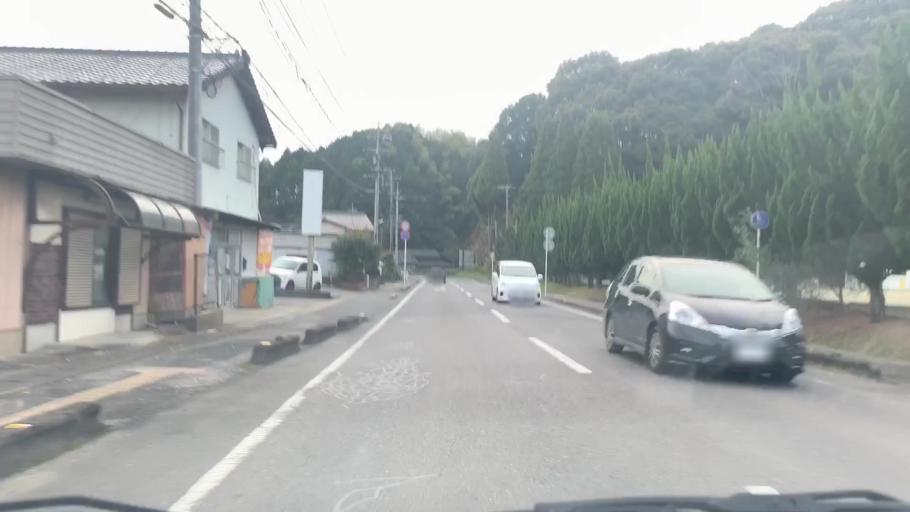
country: JP
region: Saga Prefecture
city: Takeocho-takeo
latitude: 33.1924
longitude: 130.0315
